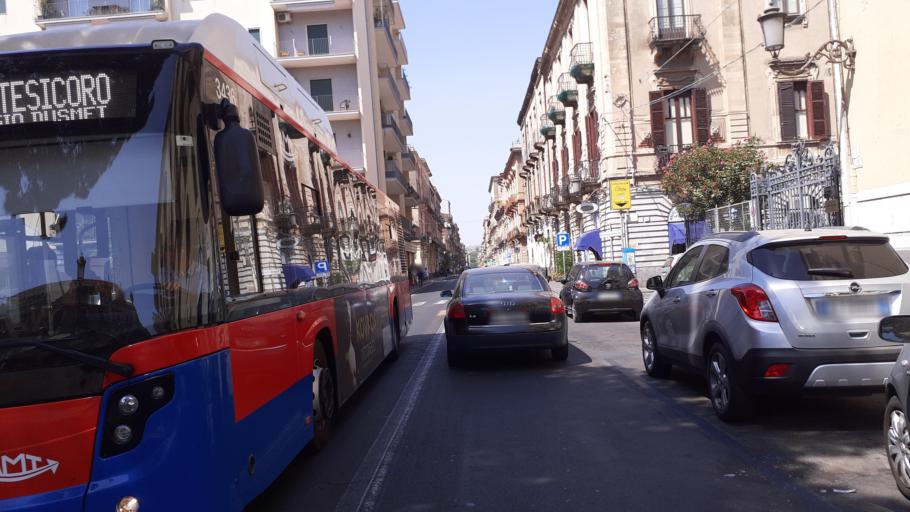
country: IT
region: Sicily
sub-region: Catania
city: Canalicchio
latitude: 37.5128
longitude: 15.0973
